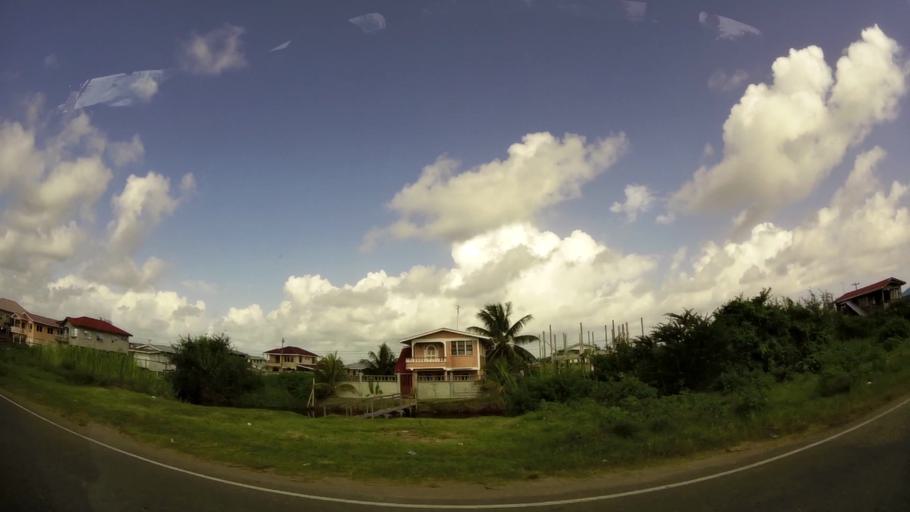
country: GY
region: Demerara-Mahaica
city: Mahaica Village
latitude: 6.7406
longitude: -57.9565
